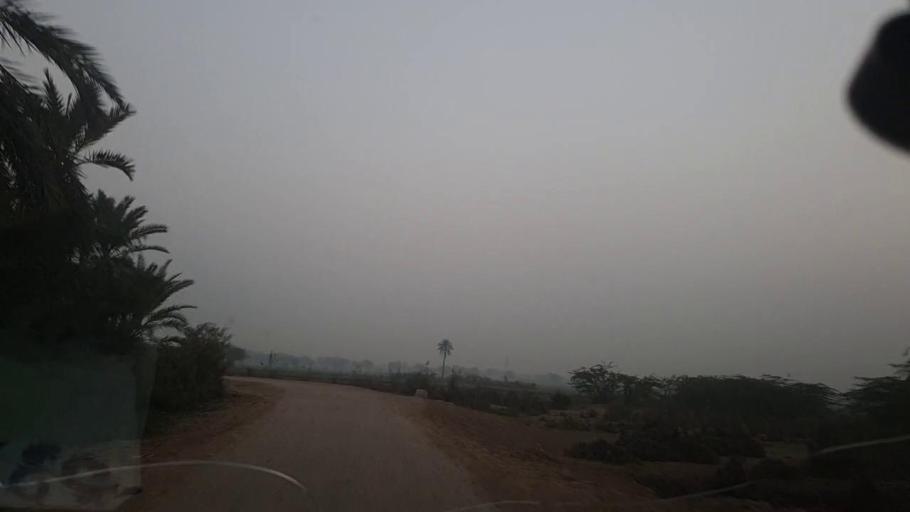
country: PK
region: Sindh
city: Hingorja
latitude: 27.2190
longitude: 68.4326
